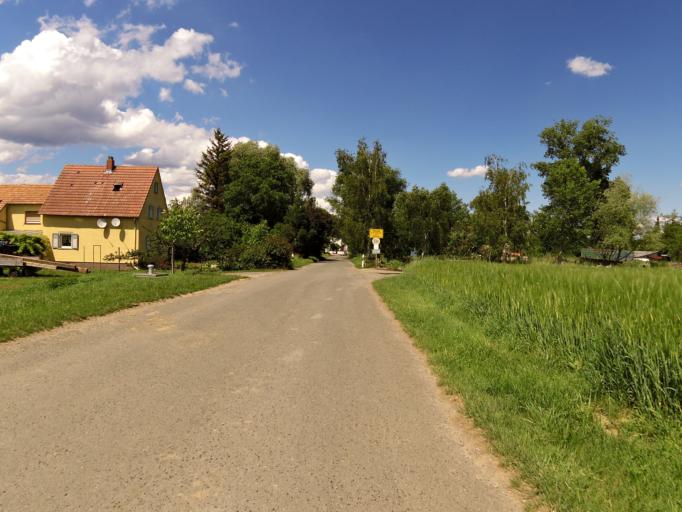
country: DE
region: Rheinland-Pfalz
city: Altdorf
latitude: 49.2970
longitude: 8.2150
